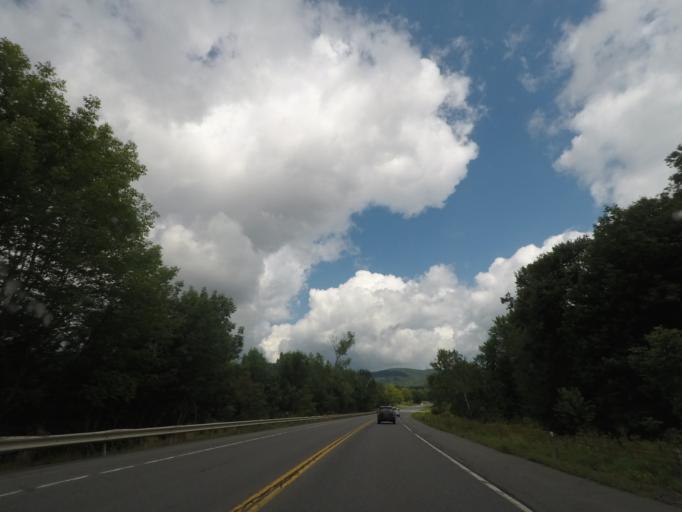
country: US
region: Massachusetts
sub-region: Berkshire County
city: Lanesborough
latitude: 42.6093
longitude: -73.3757
